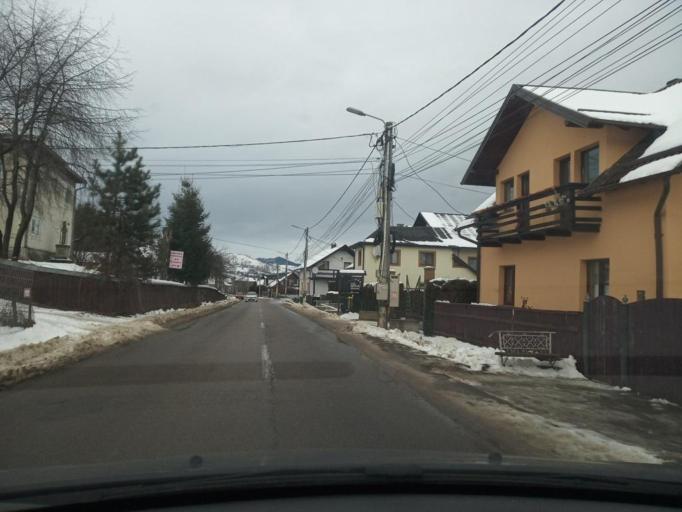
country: RO
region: Suceava
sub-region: Oras Gura Humorului
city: Gura Humorului
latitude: 47.5338
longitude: 25.8645
